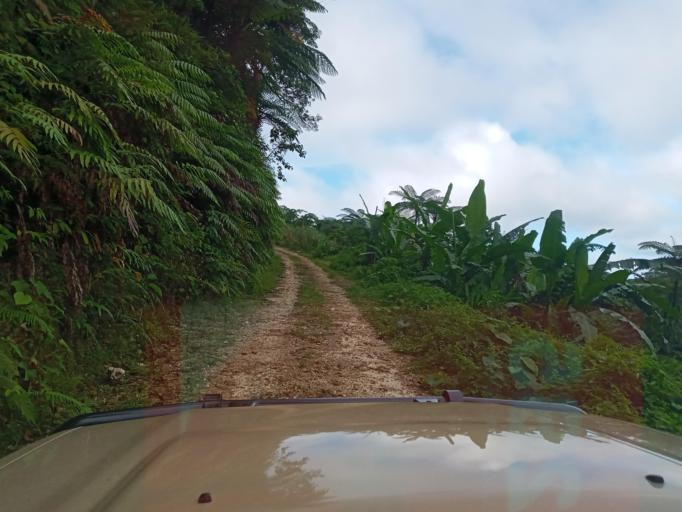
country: VU
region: Penama
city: Saratamata
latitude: -15.9720
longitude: 168.2507
